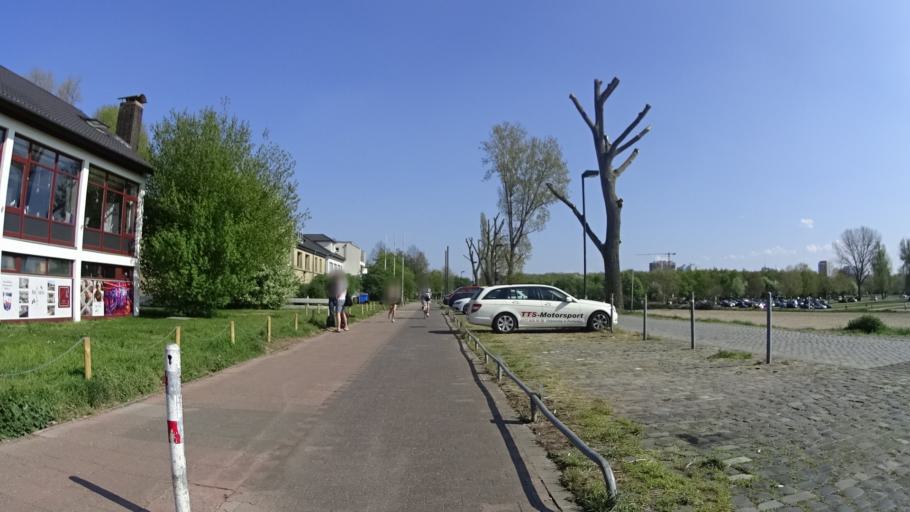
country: DE
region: North Rhine-Westphalia
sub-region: Regierungsbezirk Dusseldorf
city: Dusseldorf
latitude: 51.2512
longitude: 6.7298
